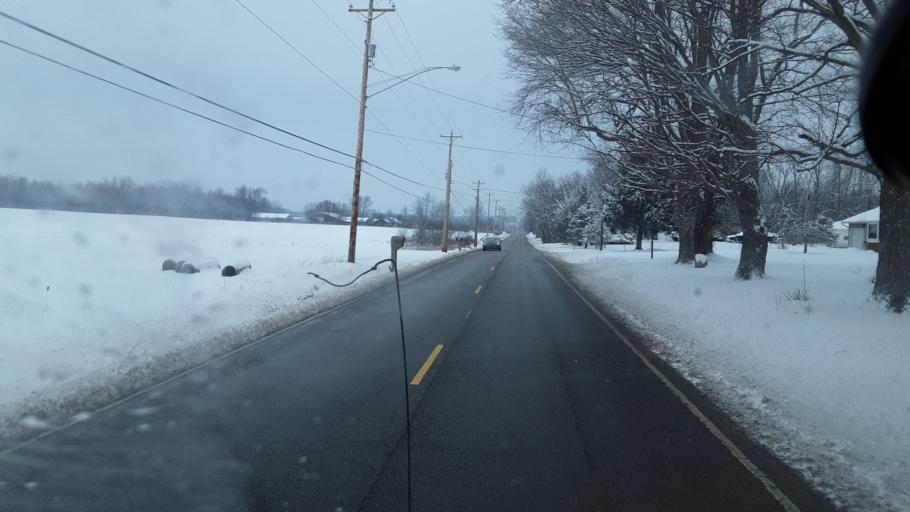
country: US
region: Ohio
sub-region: Licking County
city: Heath
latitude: 40.0138
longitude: -82.4811
